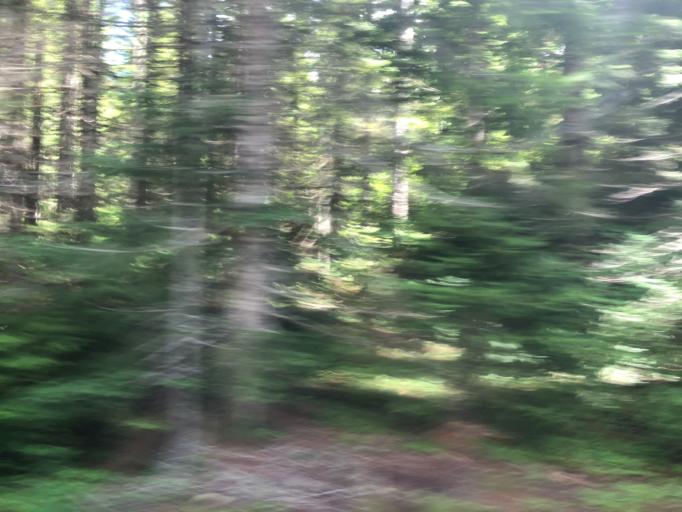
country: US
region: Oregon
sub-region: Clackamas County
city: Mount Hood Village
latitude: 45.4685
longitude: -121.8536
